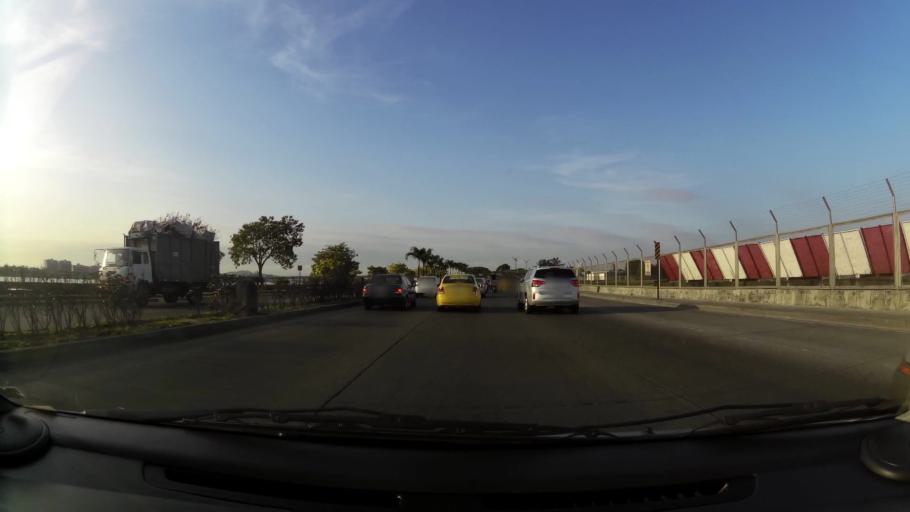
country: EC
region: Guayas
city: Eloy Alfaro
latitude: -2.1459
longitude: -79.8768
